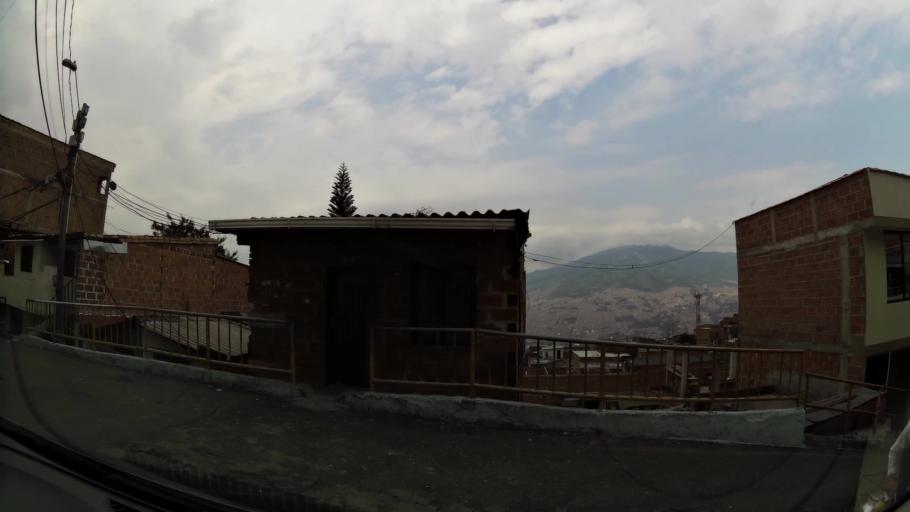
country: CO
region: Antioquia
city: Medellin
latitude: 6.2857
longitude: -75.5461
